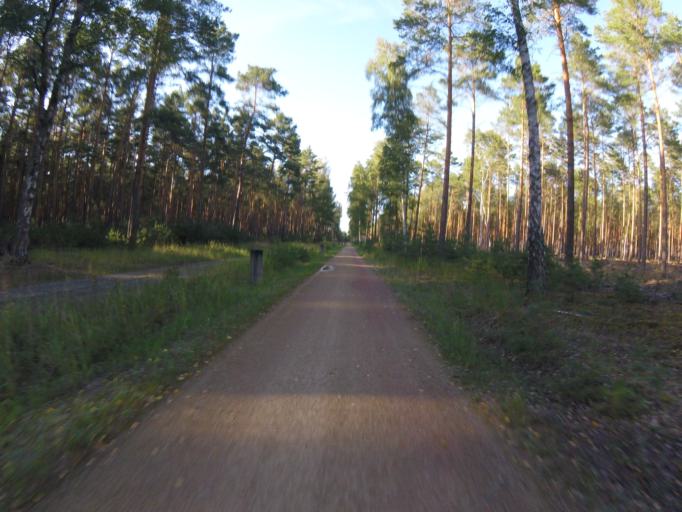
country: DE
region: Brandenburg
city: Halbe
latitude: 52.1911
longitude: 13.7616
